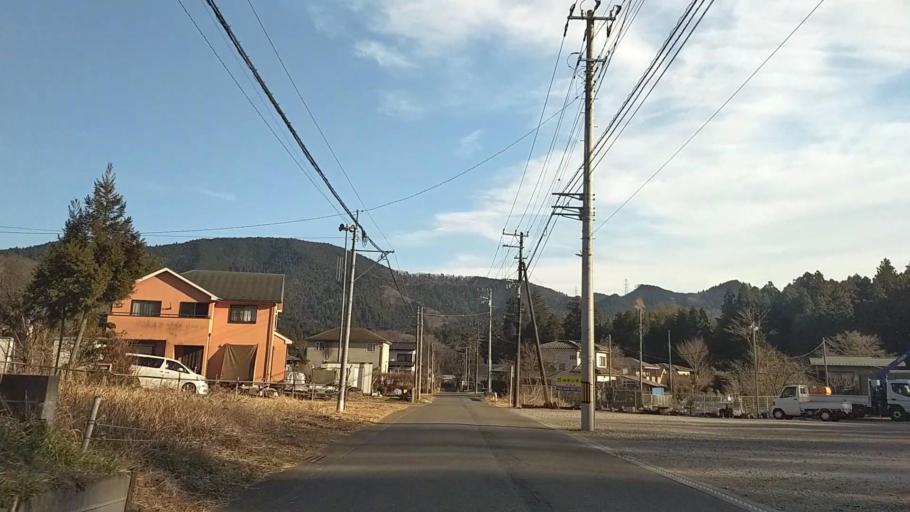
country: JP
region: Yamanashi
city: Uenohara
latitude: 35.5490
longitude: 139.2162
